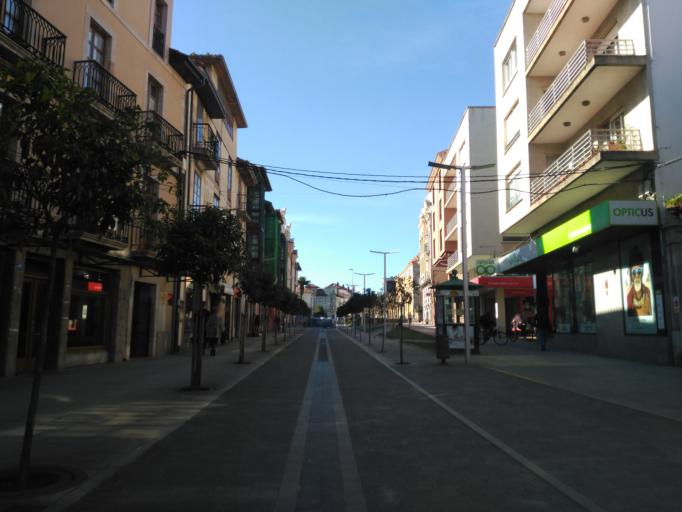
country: ES
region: Asturias
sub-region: Province of Asturias
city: Llanes
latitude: 43.4211
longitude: -4.7558
